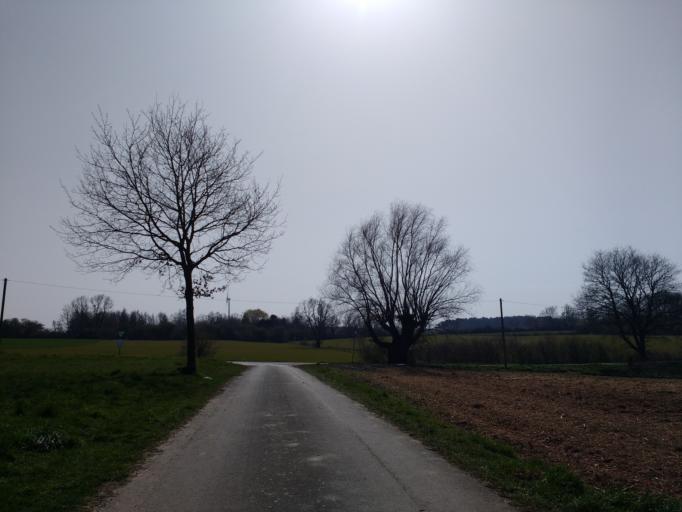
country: DE
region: North Rhine-Westphalia
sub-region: Regierungsbezirk Detmold
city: Salzkotten
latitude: 51.7282
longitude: 8.6474
